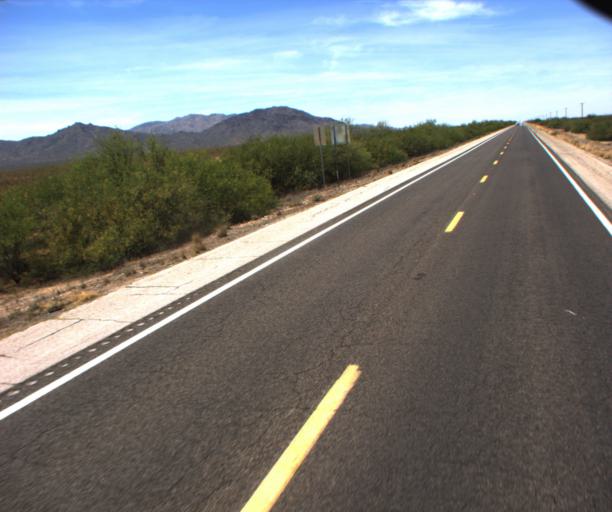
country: US
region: Arizona
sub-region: Yavapai County
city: Congress
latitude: 33.9325
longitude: -113.2129
